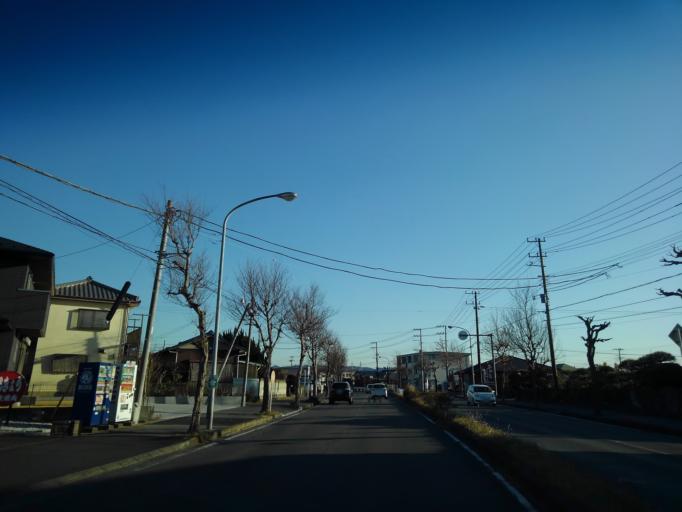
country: JP
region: Chiba
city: Kimitsu
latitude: 35.3231
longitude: 139.9112
